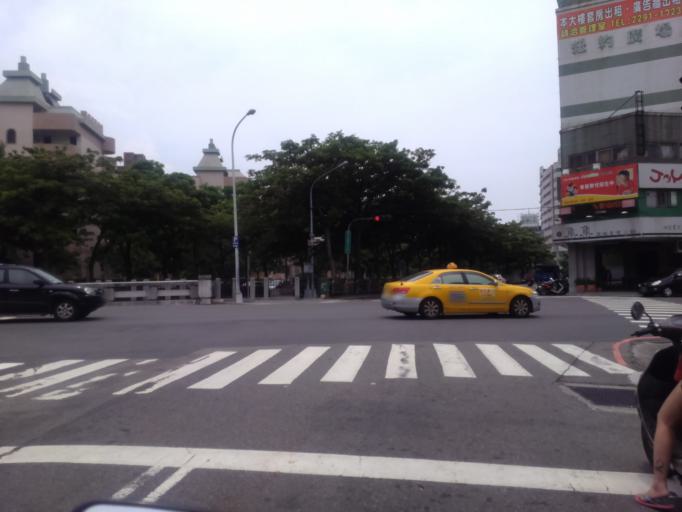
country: TW
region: Taiwan
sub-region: Taichung City
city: Taichung
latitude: 24.1672
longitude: 120.6779
